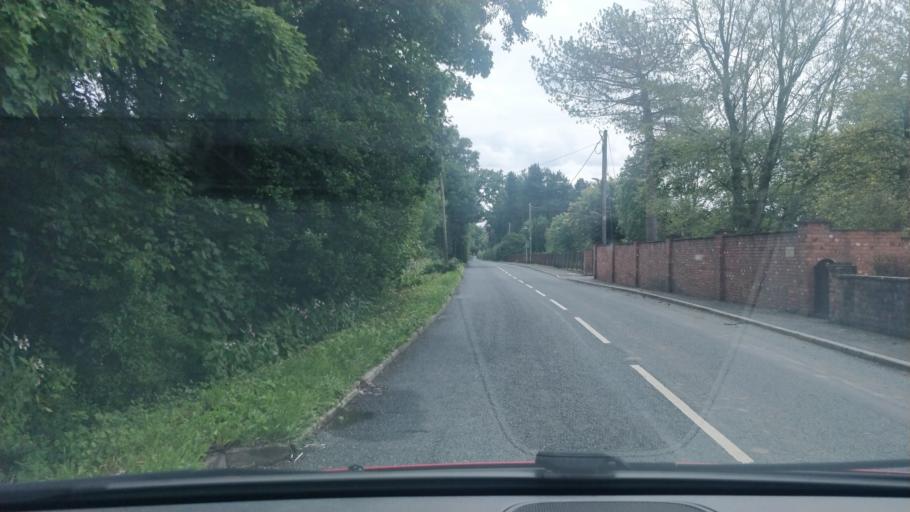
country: GB
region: England
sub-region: Lancashire
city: Croston
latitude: 53.6989
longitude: -2.7429
